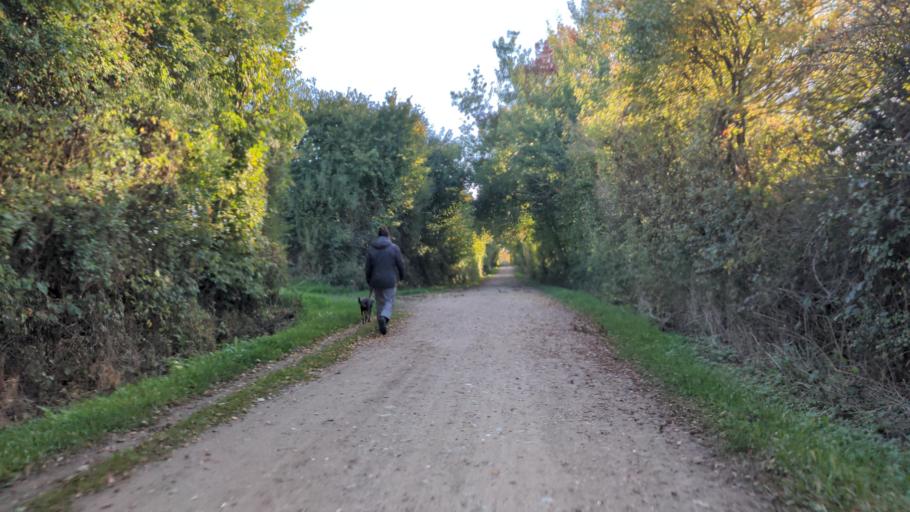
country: DE
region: Schleswig-Holstein
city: Neustadt in Holstein
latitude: 54.0961
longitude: 10.8468
